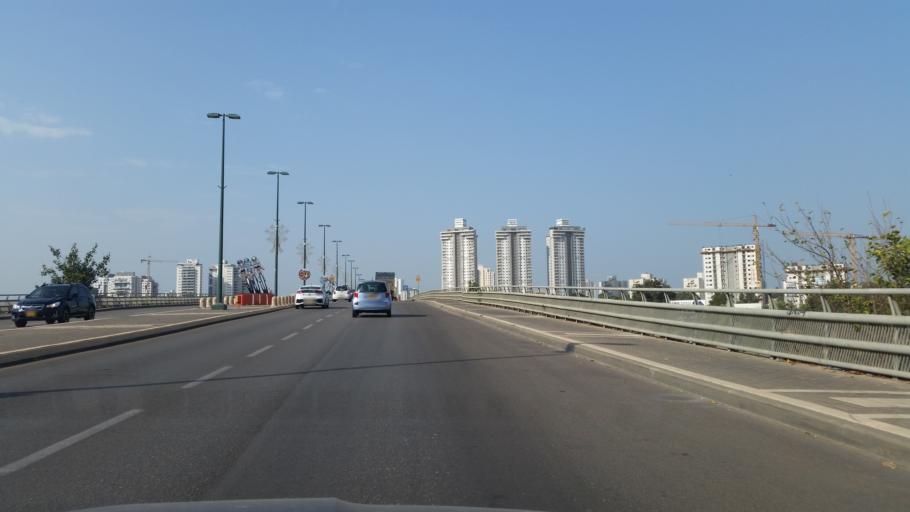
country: IL
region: Central District
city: Netanya
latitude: 32.3122
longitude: 34.8690
